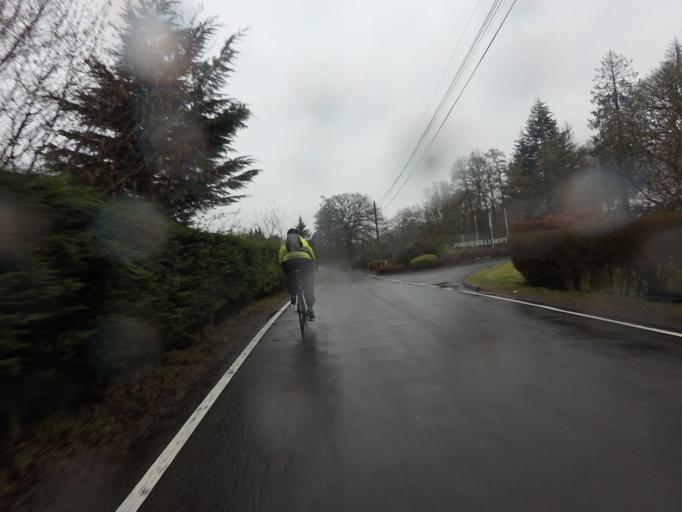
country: GB
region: Scotland
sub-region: Stirling
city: Killearn
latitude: 56.1877
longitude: -4.4793
